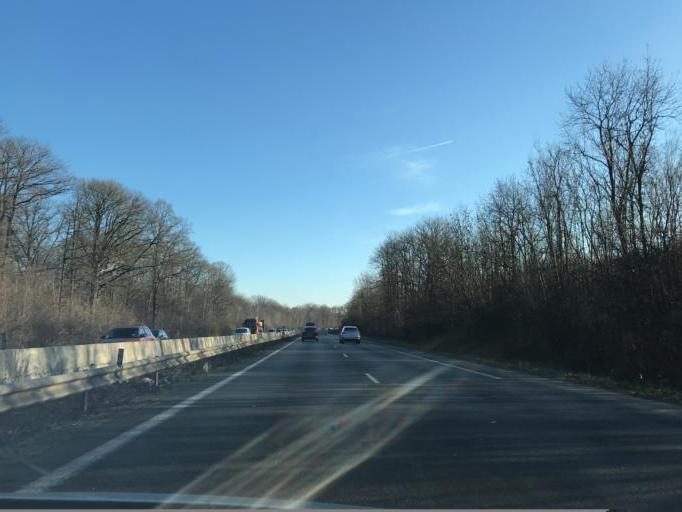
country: FR
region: Ile-de-France
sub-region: Departement de Seine-et-Marne
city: Lesigny
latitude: 48.7668
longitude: 2.6137
